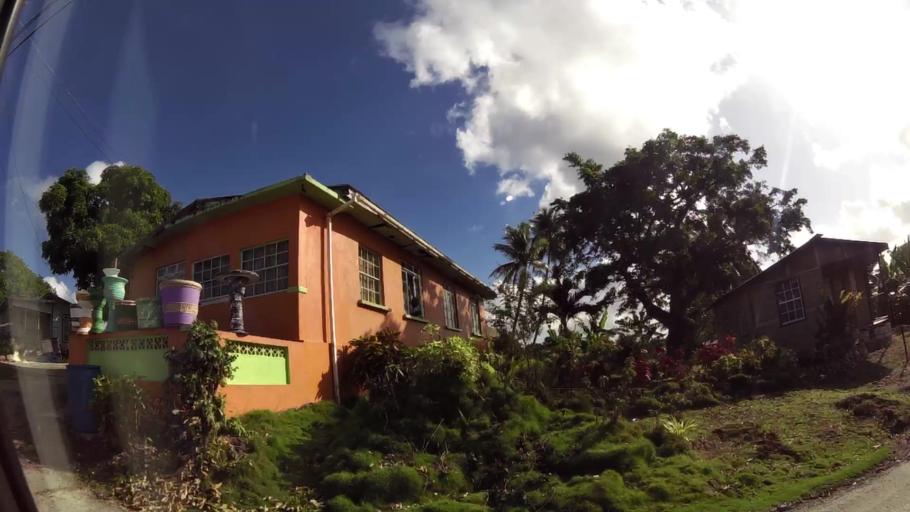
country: BB
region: Saint James
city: Holetown
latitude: 13.1537
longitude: -59.6069
